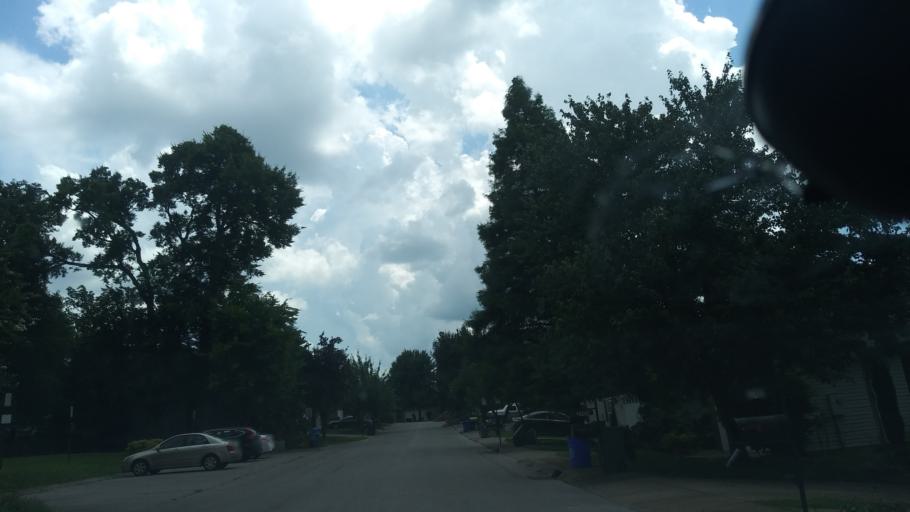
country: US
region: Tennessee
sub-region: Davidson County
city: Oak Hill
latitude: 36.1240
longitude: -86.7631
